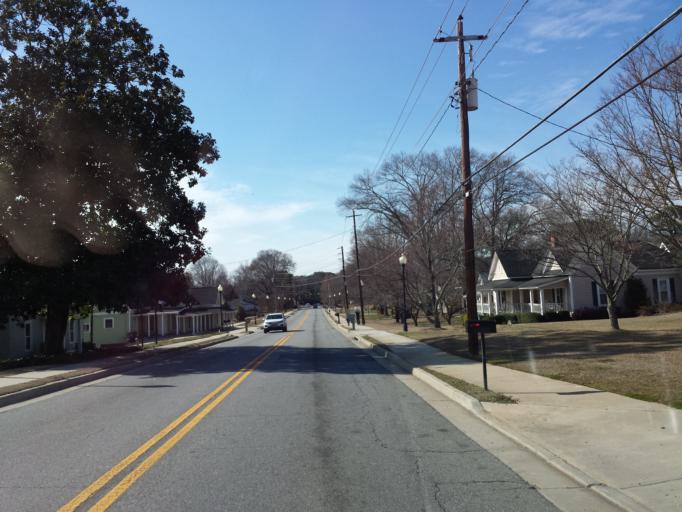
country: US
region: Georgia
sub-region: Cobb County
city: Kennesaw
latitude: 34.0256
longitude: -84.6196
